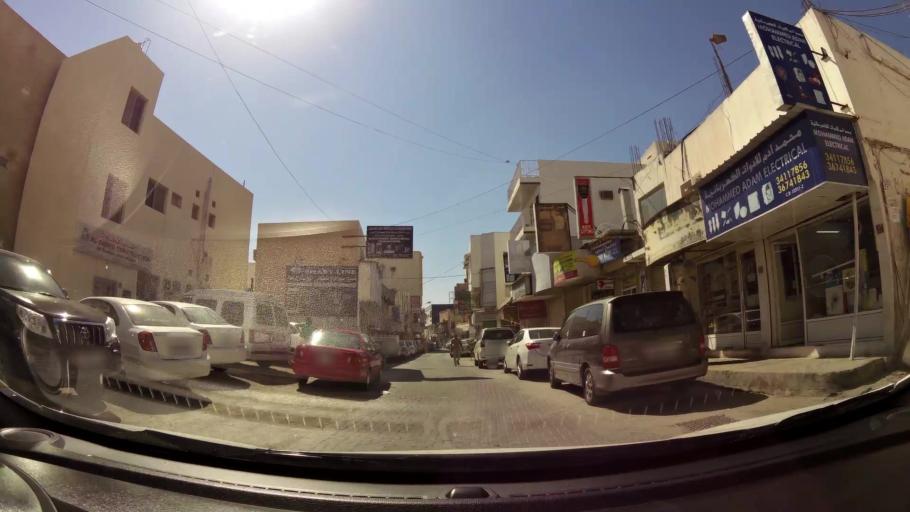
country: BH
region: Muharraq
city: Al Muharraq
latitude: 26.2498
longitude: 50.6100
